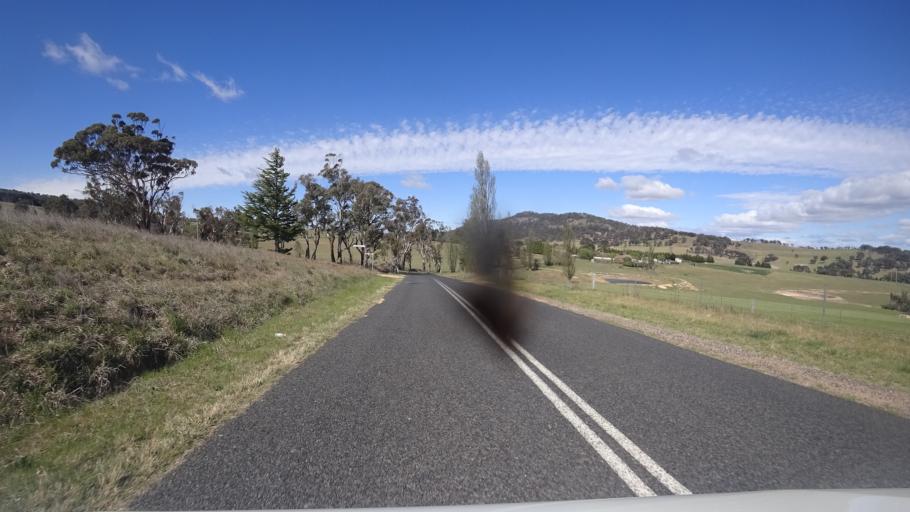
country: AU
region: New South Wales
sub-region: Lithgow
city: Portland
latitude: -33.5211
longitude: 149.9457
